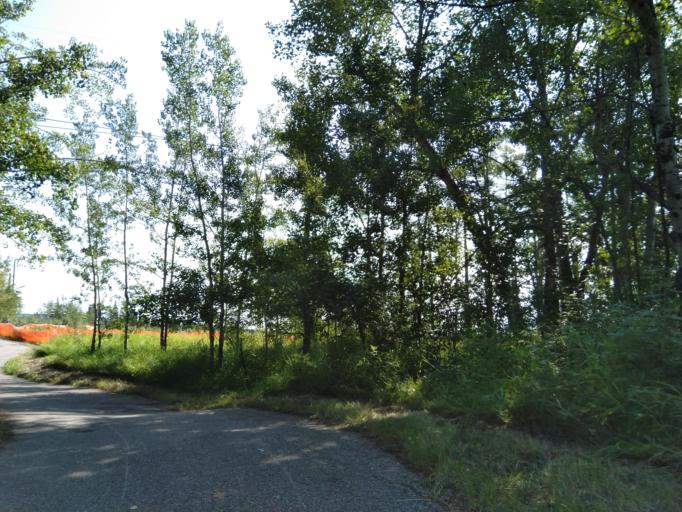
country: CA
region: Alberta
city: Calgary
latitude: 51.0955
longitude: -114.2360
